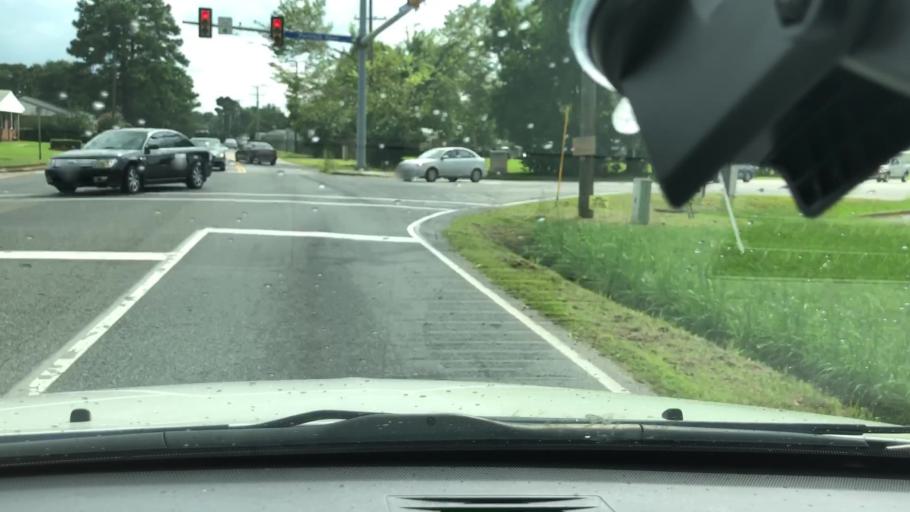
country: US
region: Virginia
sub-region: City of Chesapeake
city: Chesapeake
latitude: 36.7859
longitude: -76.2661
